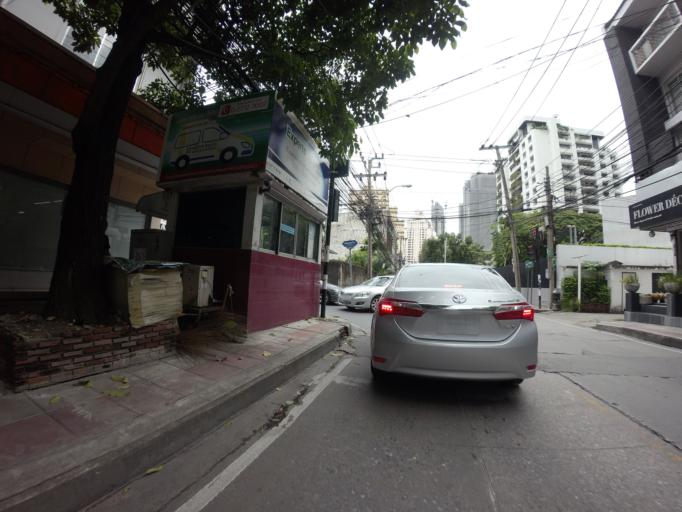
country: TH
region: Bangkok
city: Watthana
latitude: 13.7365
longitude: 100.5718
